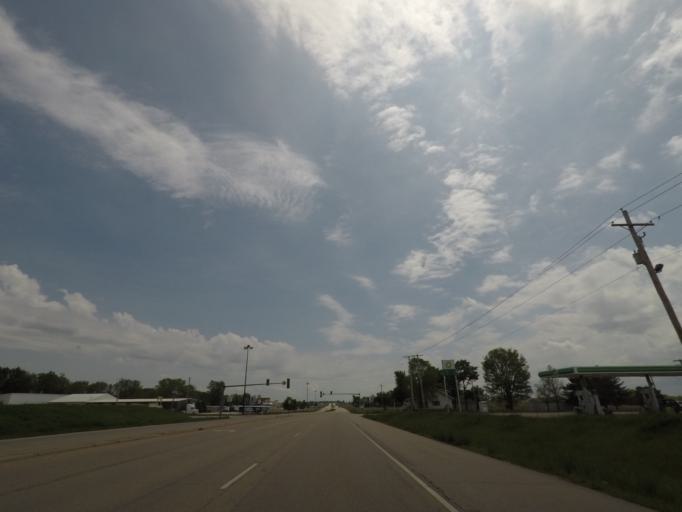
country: US
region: Illinois
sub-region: McLean County
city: Bloomington
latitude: 40.4307
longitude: -88.9906
